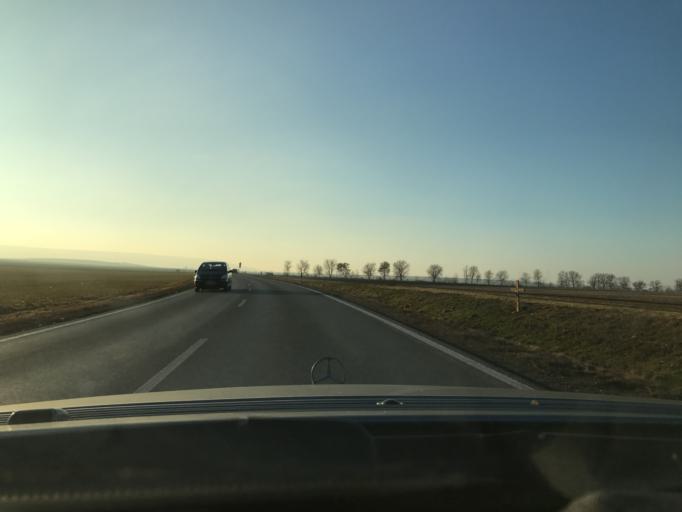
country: DE
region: Thuringia
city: Andisleben
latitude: 51.0840
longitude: 10.9071
